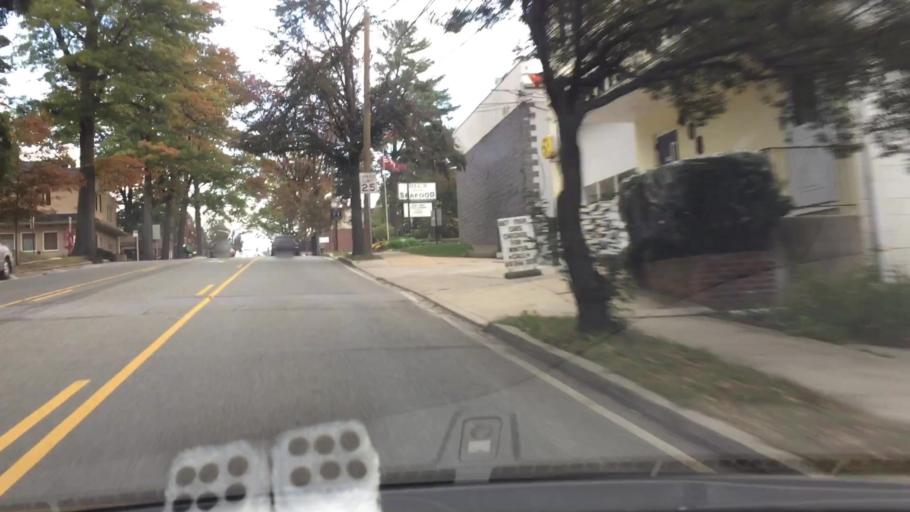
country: US
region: Pennsylvania
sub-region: Delaware County
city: Media
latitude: 39.9177
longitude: -75.3959
